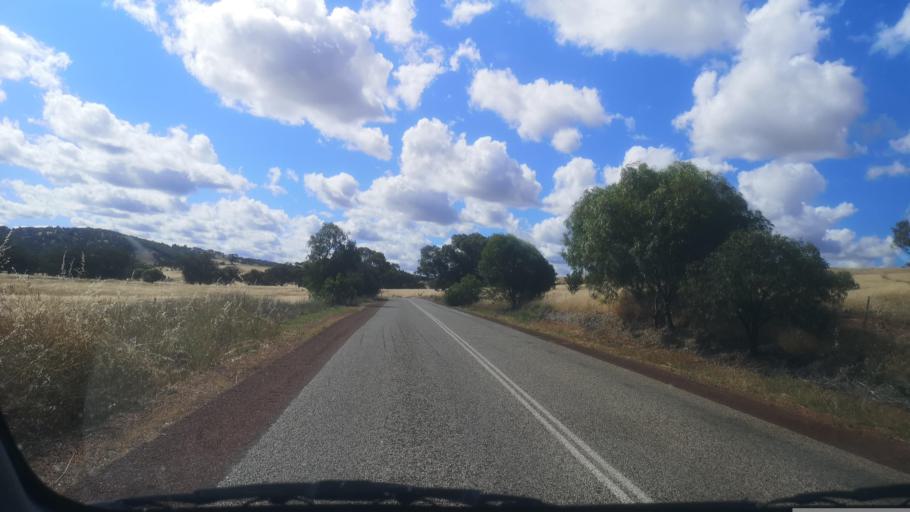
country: AU
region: Western Australia
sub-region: Toodyay
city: Toodyay
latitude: -31.5023
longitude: 116.4472
